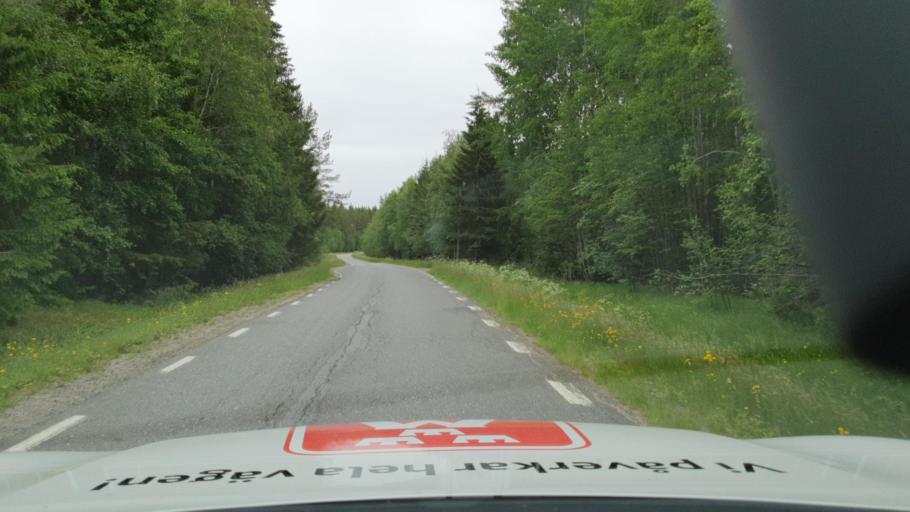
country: SE
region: Vaesterbotten
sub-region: Nordmalings Kommun
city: Nordmaling
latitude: 63.4820
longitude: 19.4519
